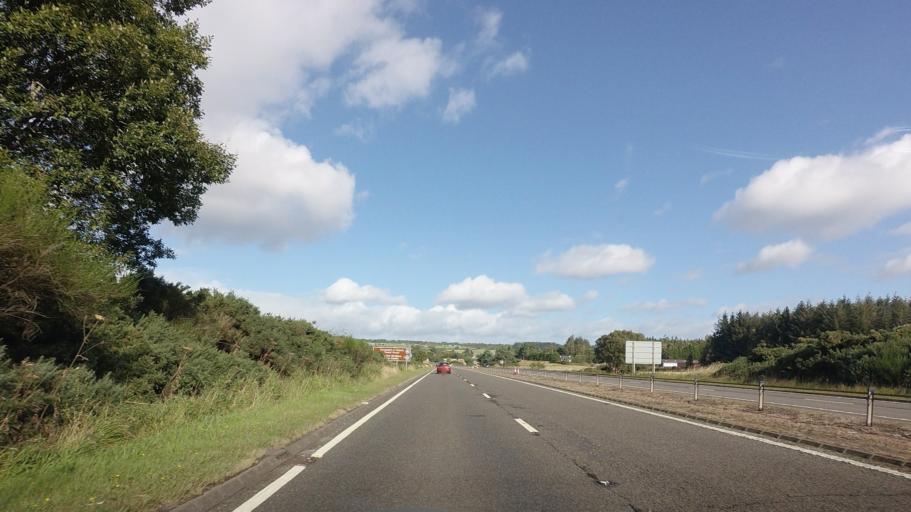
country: GB
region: Scotland
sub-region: Highland
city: Conon Bridge
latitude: 57.5324
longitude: -4.3280
